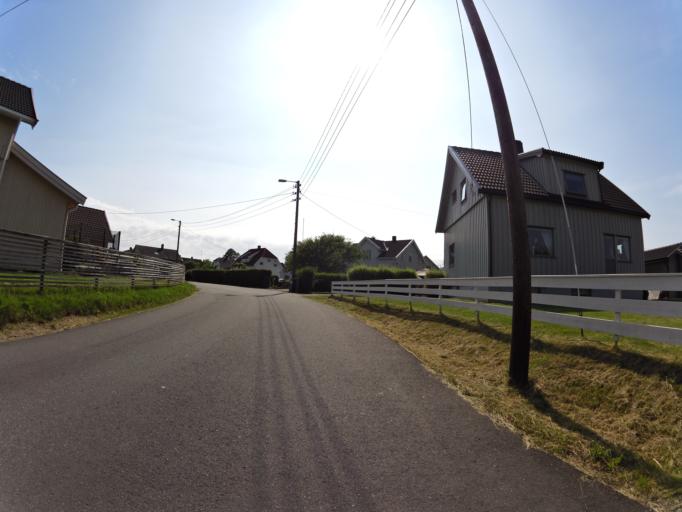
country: NO
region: Ostfold
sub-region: Sarpsborg
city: Sarpsborg
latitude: 59.2683
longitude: 11.0214
